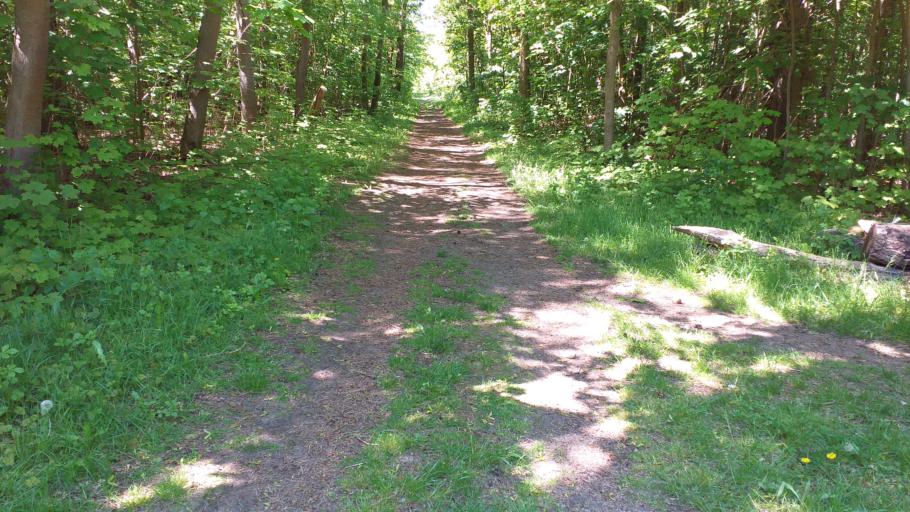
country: NL
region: North Holland
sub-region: Gemeente Castricum
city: Castricum
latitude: 52.5363
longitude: 4.6344
